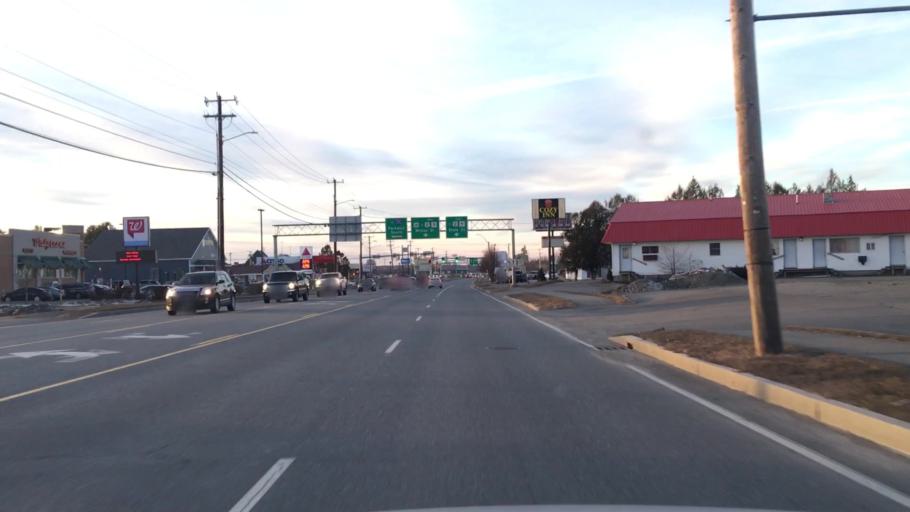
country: US
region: Maine
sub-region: Penobscot County
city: Brewer
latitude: 44.7828
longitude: -68.7482
